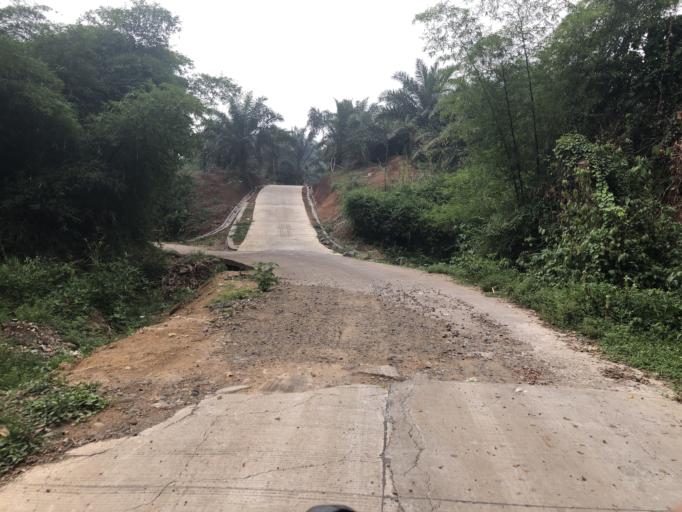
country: ID
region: West Java
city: Ciampea
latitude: -6.5495
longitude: 106.7154
